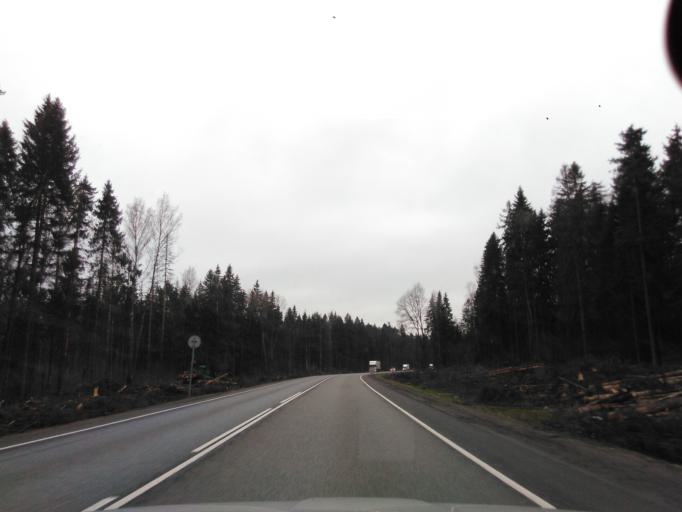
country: RU
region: Moskovskaya
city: Povarovo
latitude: 55.9941
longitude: 37.0224
